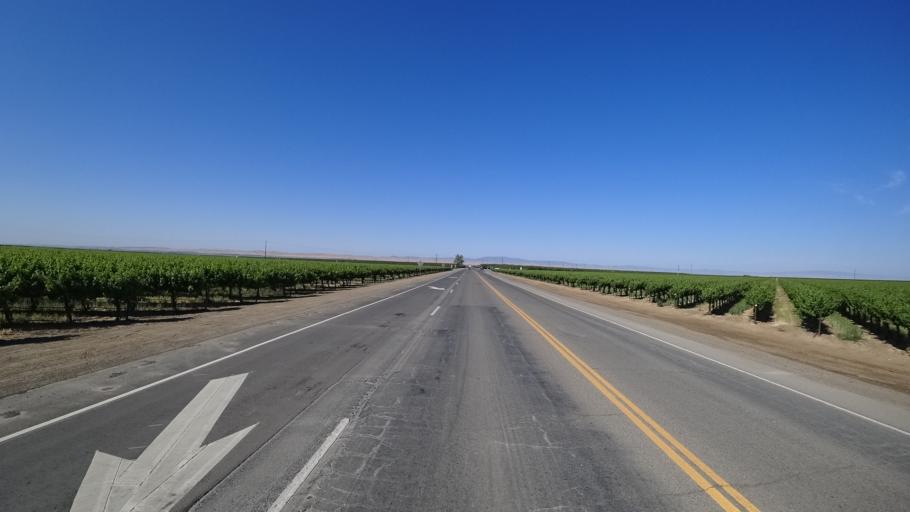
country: US
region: California
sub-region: Fresno County
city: Huron
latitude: 36.1397
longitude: -120.0089
